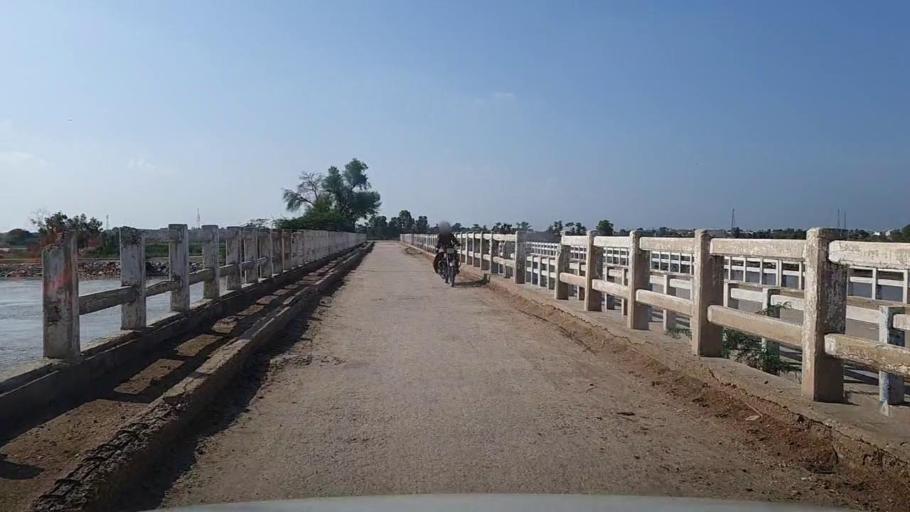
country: PK
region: Sindh
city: Kandiaro
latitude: 27.0727
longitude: 68.3134
